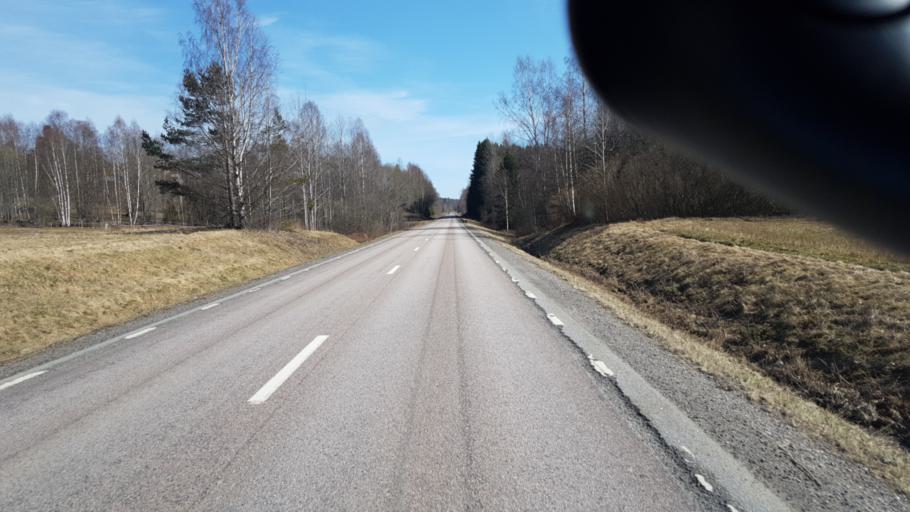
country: SE
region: Vaermland
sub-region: Arvika Kommun
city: Arvika
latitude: 59.6347
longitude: 12.8014
